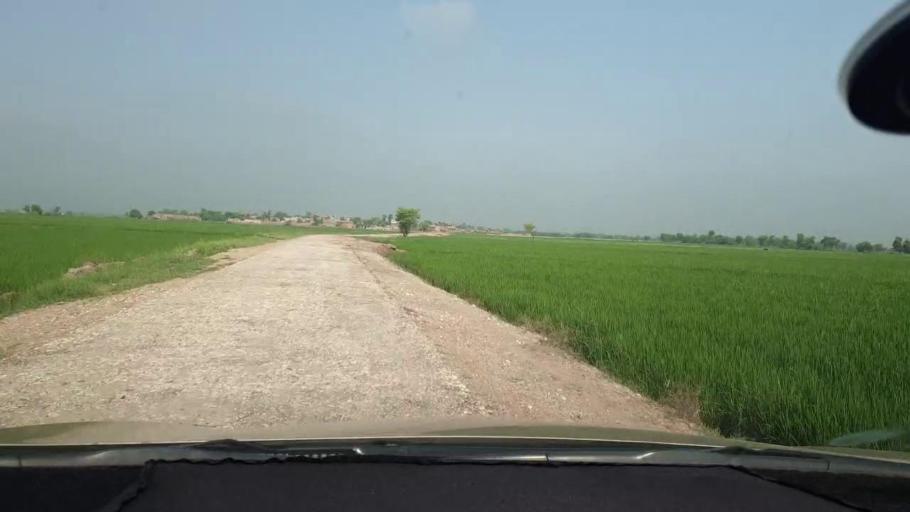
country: PK
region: Sindh
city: Kambar
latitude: 27.5397
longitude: 68.0523
